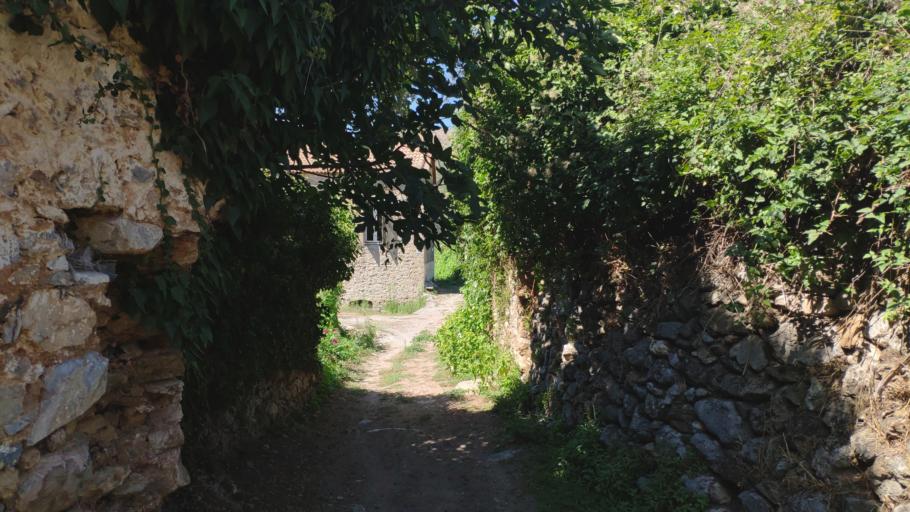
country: GR
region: Peloponnese
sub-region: Nomos Lakonias
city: Kariai
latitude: 37.1752
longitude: 22.5930
